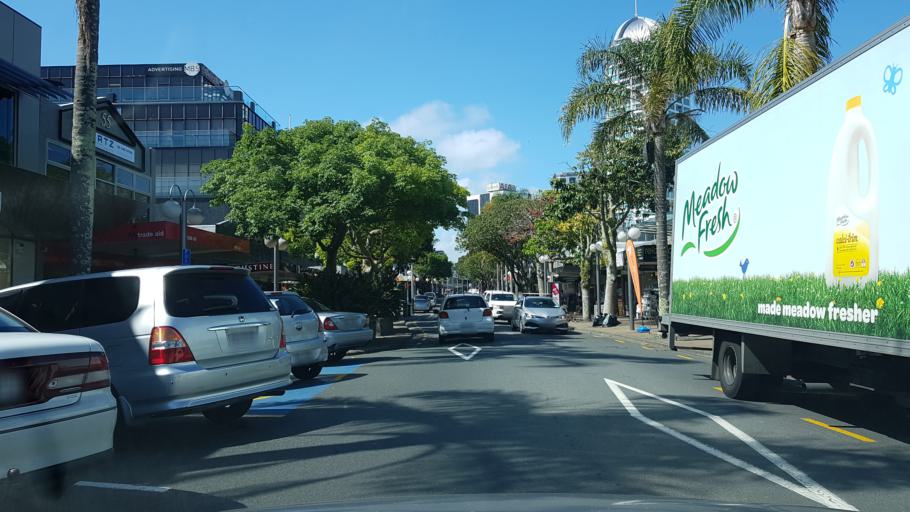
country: NZ
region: Auckland
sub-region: Auckland
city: North Shore
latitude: -36.7869
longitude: 174.7728
